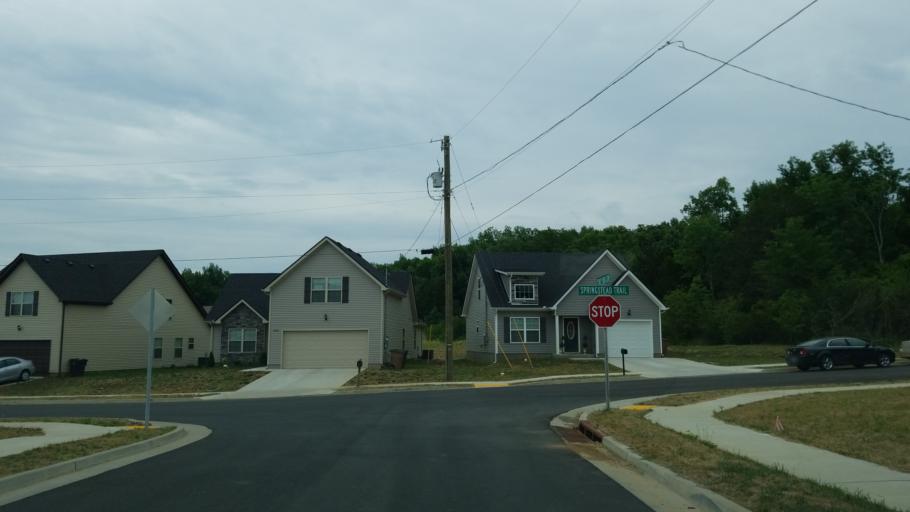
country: US
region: Tennessee
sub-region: Rutherford County
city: La Vergne
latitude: 36.0509
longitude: -86.5958
